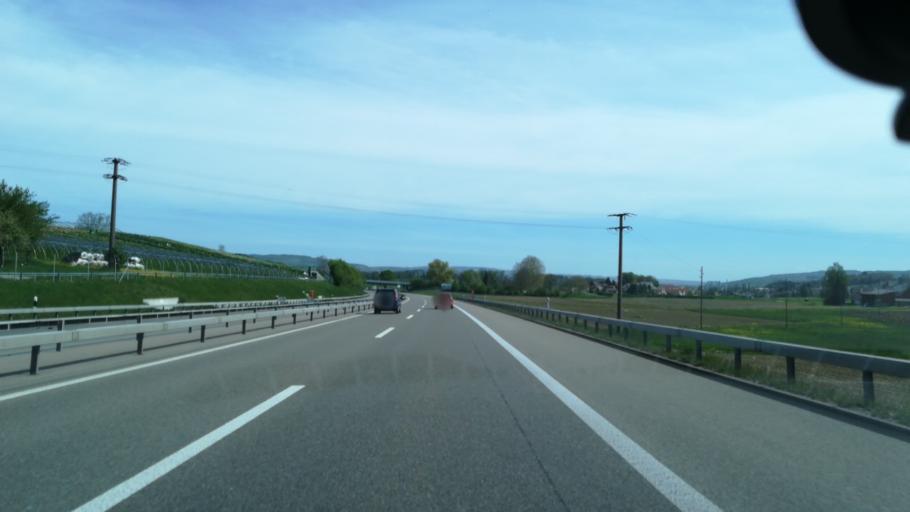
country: CH
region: Zurich
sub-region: Bezirk Winterthur
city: Sulz
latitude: 47.5434
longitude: 8.8182
